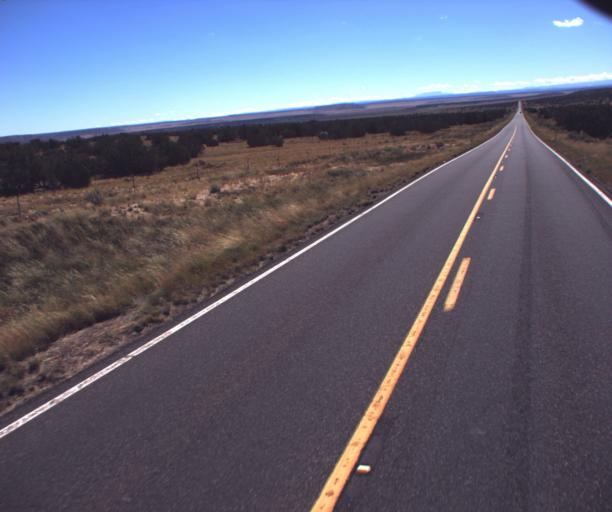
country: US
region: Arizona
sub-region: Apache County
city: Saint Johns
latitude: 34.8161
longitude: -109.2376
